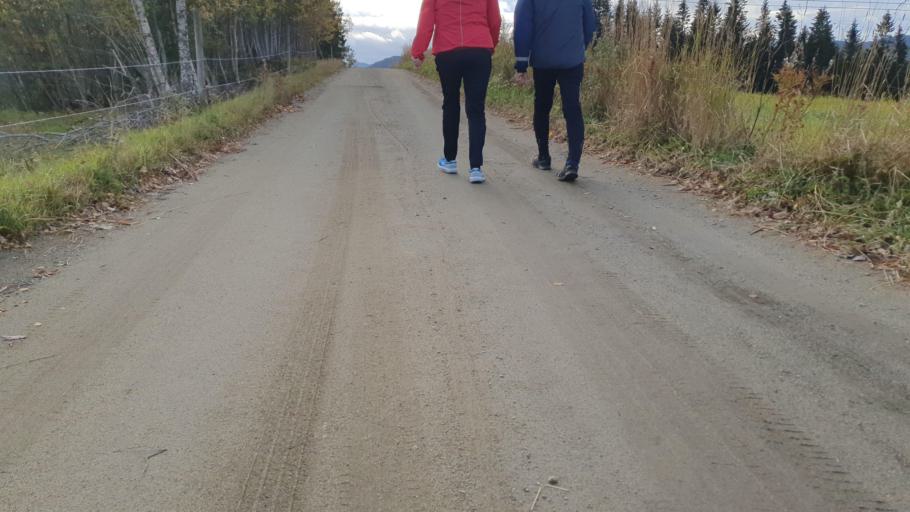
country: NO
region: Sor-Trondelag
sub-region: Klaebu
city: Klaebu
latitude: 63.2935
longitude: 10.4632
